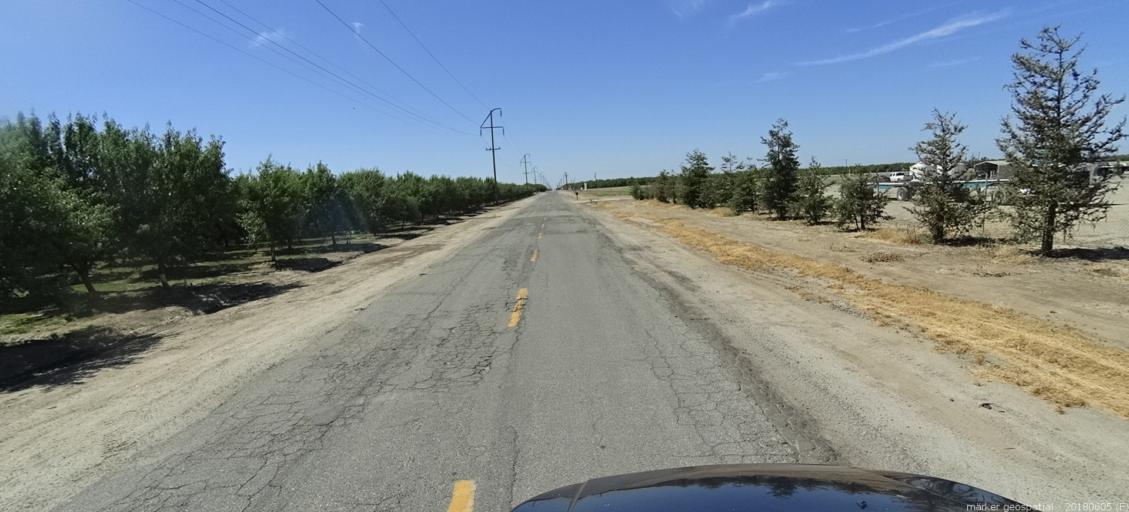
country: US
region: California
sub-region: Madera County
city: Chowchilla
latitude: 37.1157
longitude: -120.3471
